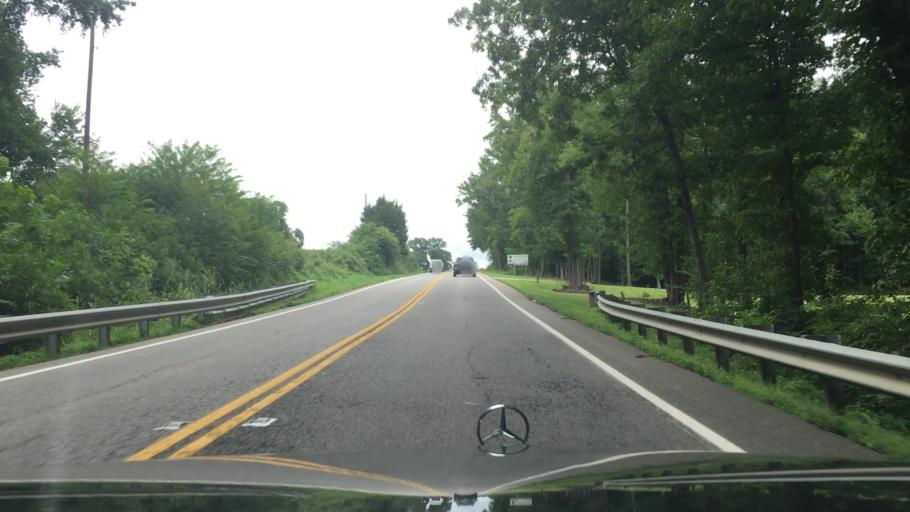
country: US
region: Virginia
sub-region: Nottoway County
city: Crewe
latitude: 37.2737
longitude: -78.1409
